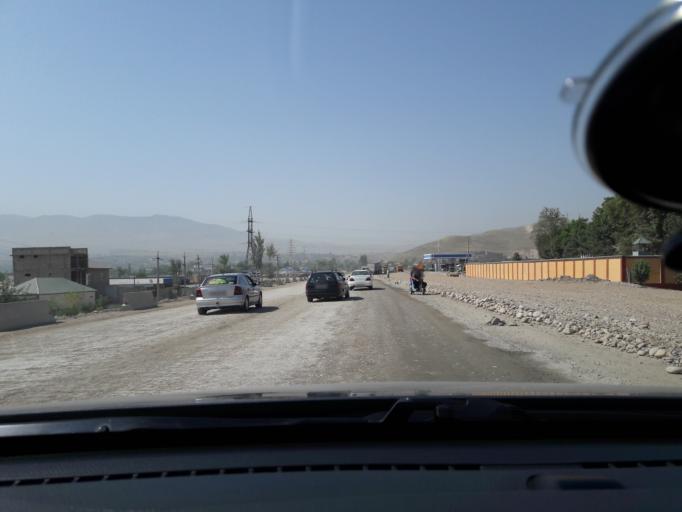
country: TJ
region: Dushanbe
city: Boshkengash
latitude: 38.4551
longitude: 68.7358
